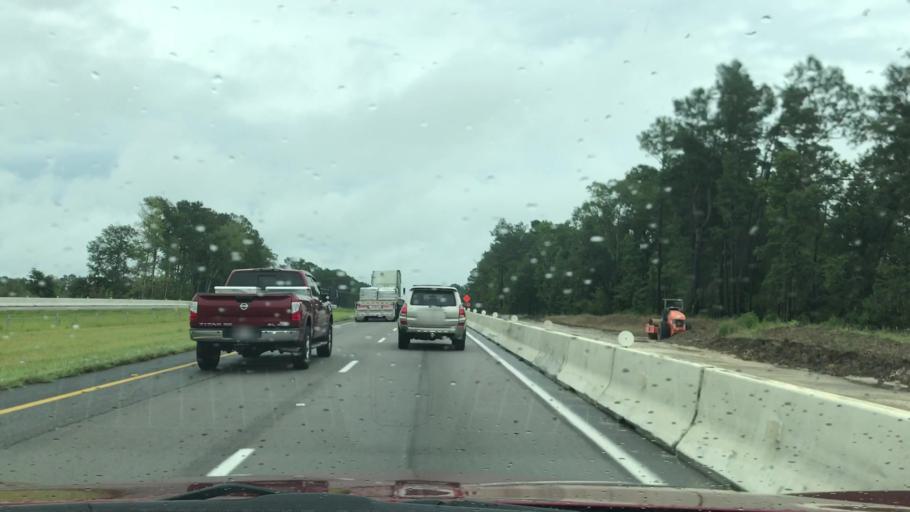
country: US
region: South Carolina
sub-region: Dorchester County
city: Ridgeville
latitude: 33.1163
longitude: -80.2693
